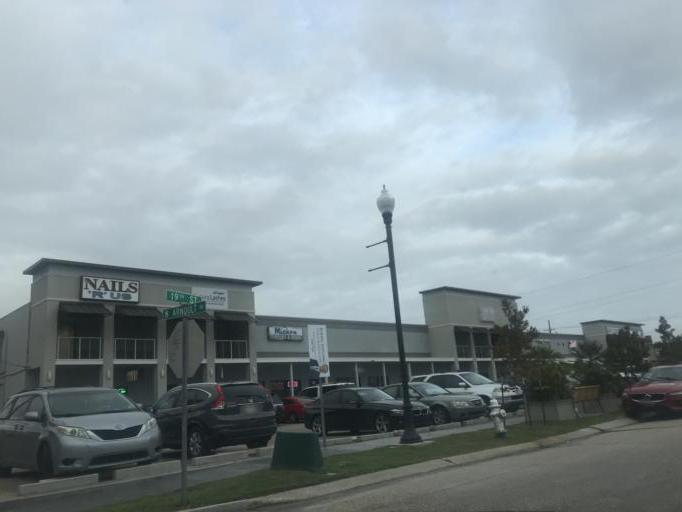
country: US
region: Louisiana
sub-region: Jefferson Parish
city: Metairie
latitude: 30.0077
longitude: -90.1604
